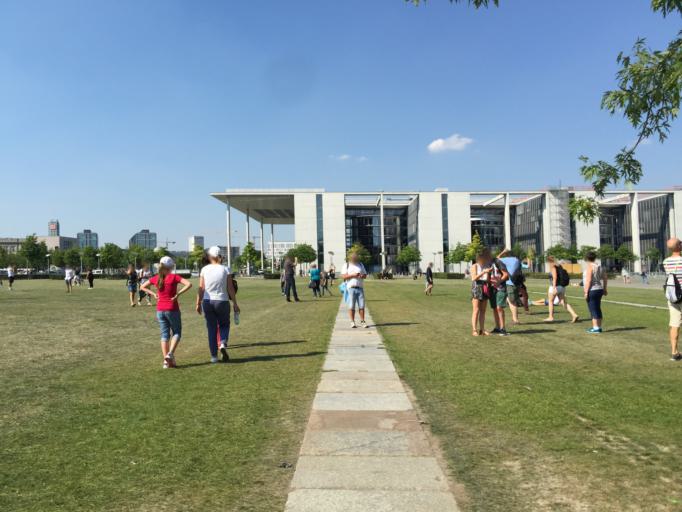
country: DE
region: Berlin
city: Tiergarten Bezirk
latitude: 52.5182
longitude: 13.3739
